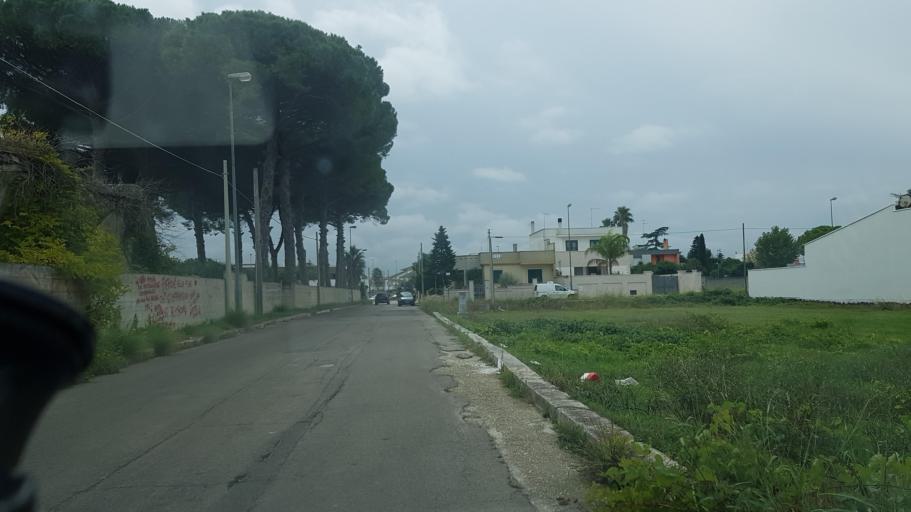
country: IT
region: Apulia
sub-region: Provincia di Brindisi
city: Cellino San Marco
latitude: 40.4757
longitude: 17.9713
